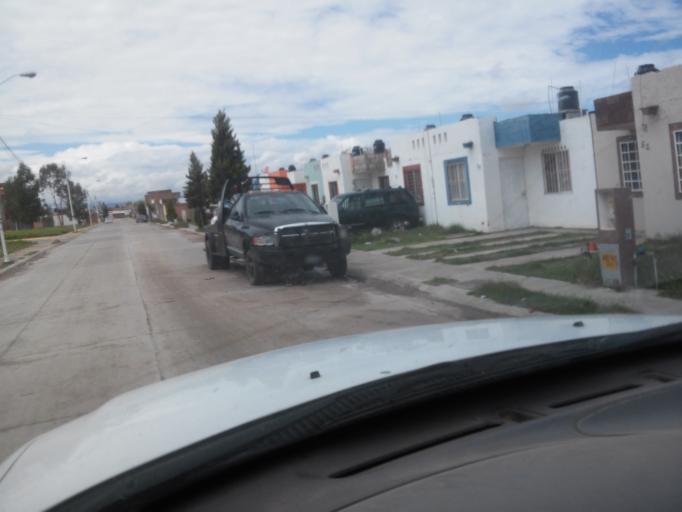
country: MX
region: Durango
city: Victoria de Durango
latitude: 24.0207
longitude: -104.6103
